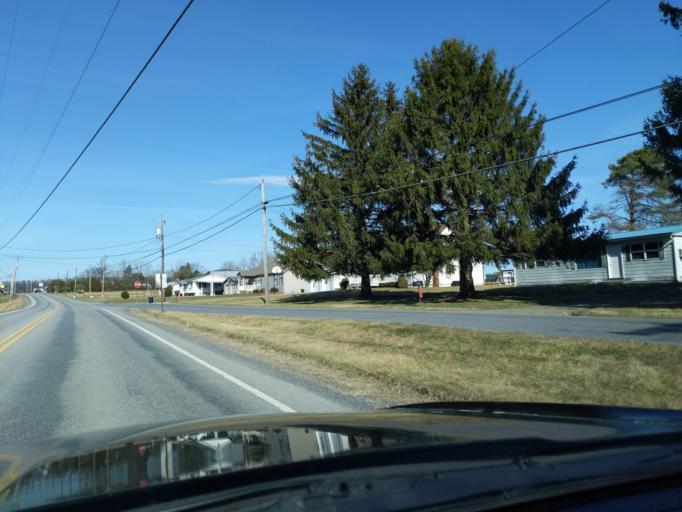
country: US
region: Pennsylvania
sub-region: Blair County
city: Martinsburg
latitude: 40.3080
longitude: -78.2856
